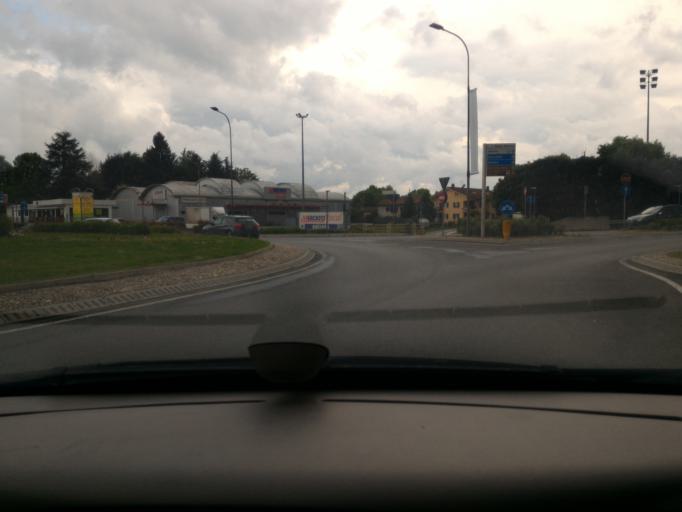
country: IT
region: Piedmont
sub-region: Provincia di Cuneo
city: Savigliano
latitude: 44.6413
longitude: 7.6505
